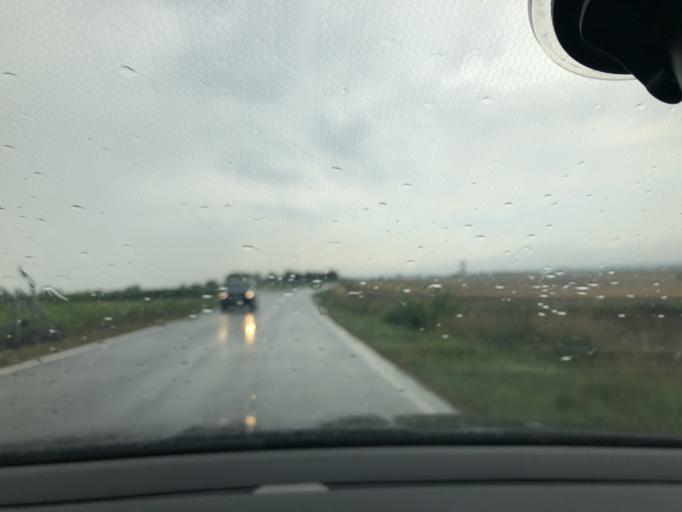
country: AT
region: Lower Austria
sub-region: Politischer Bezirk Ganserndorf
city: Auersthal
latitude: 48.3597
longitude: 16.6641
